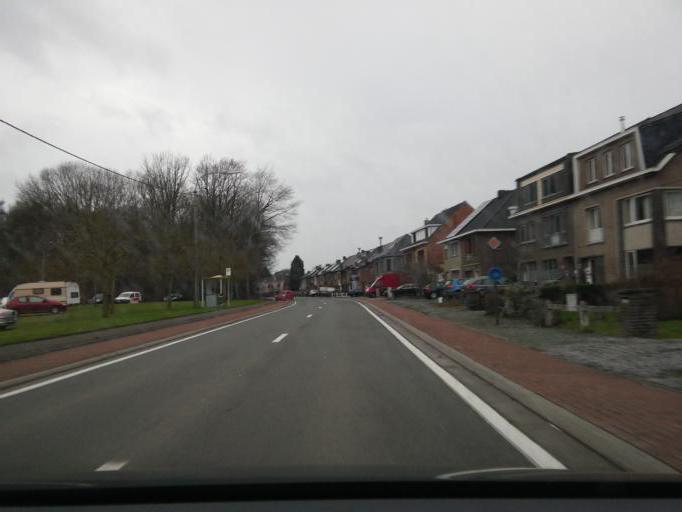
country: BE
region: Flanders
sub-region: Provincie Oost-Vlaanderen
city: Wetteren
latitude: 51.0111
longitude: 3.9070
